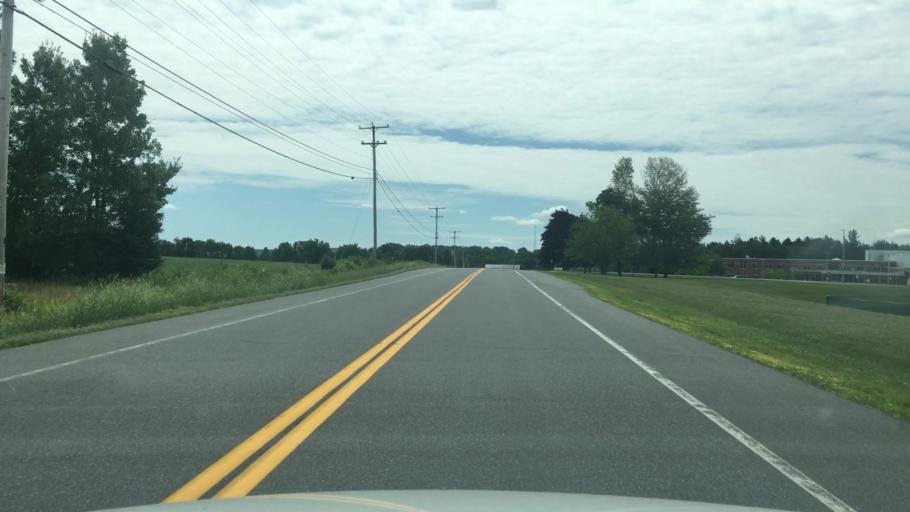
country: US
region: Maine
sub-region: Waldo County
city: Troy
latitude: 44.5539
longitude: -69.2691
